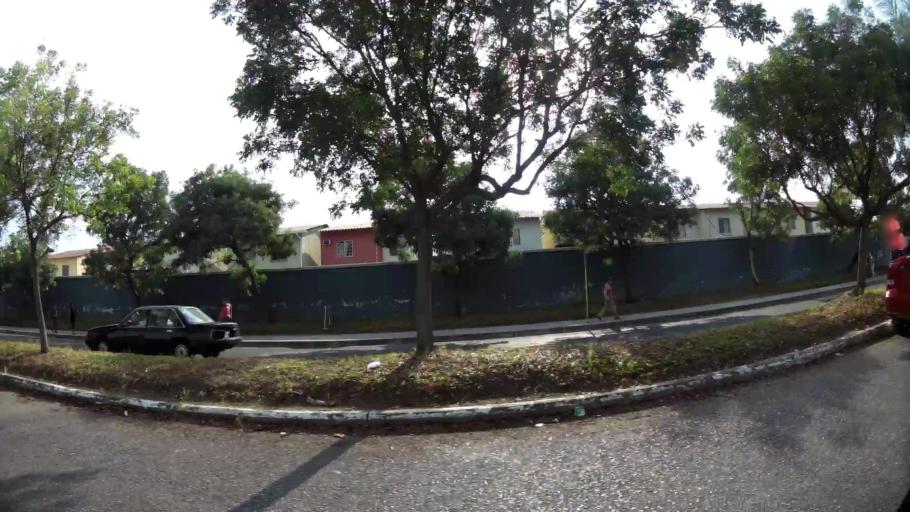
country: EC
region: Guayas
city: Eloy Alfaro
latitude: -2.0657
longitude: -79.9132
